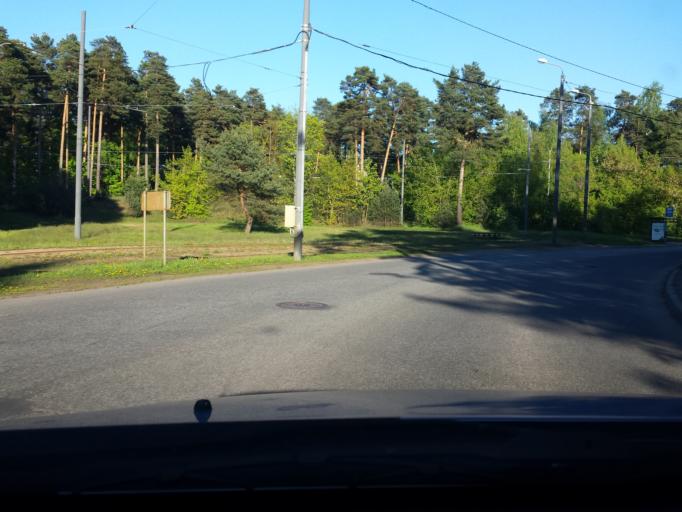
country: LV
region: Riga
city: Jaunciems
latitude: 57.0069
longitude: 24.1646
